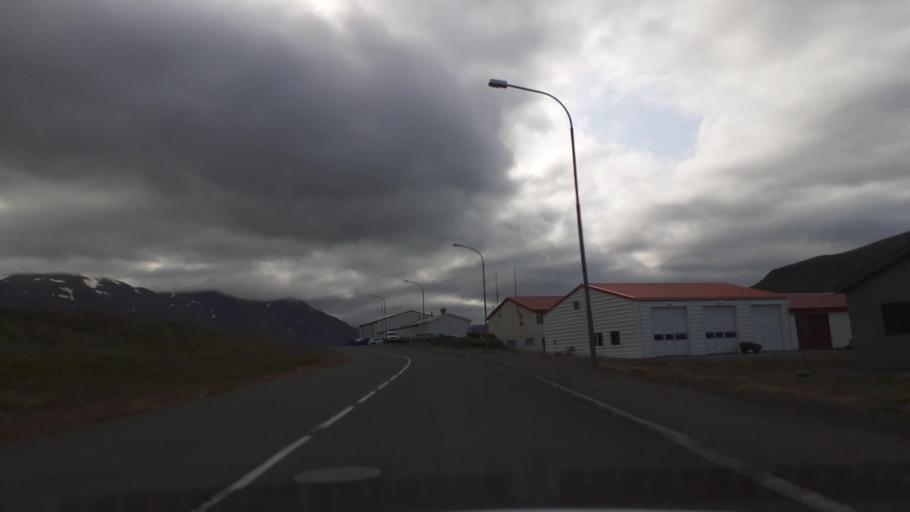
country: IS
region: Northeast
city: Akureyri
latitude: 65.9532
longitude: -18.1803
